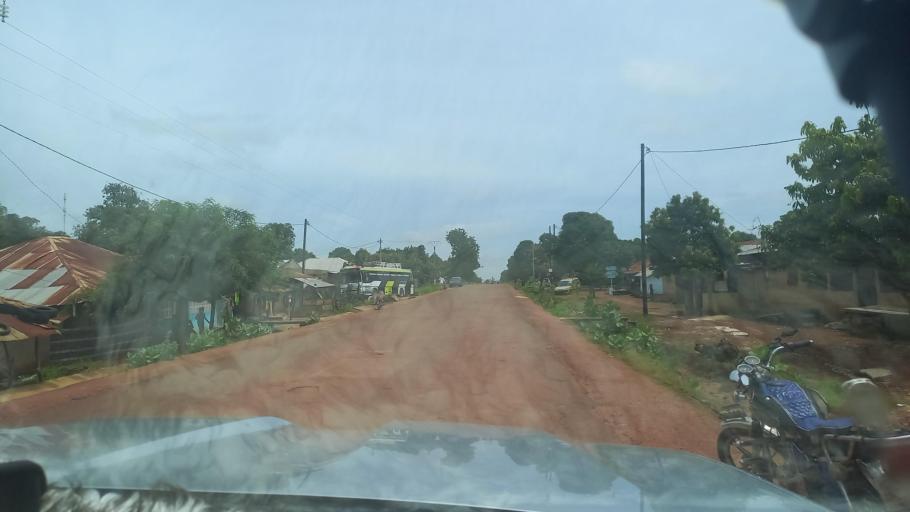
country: SN
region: Kolda
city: Marsassoum
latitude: 12.9676
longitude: -15.9569
